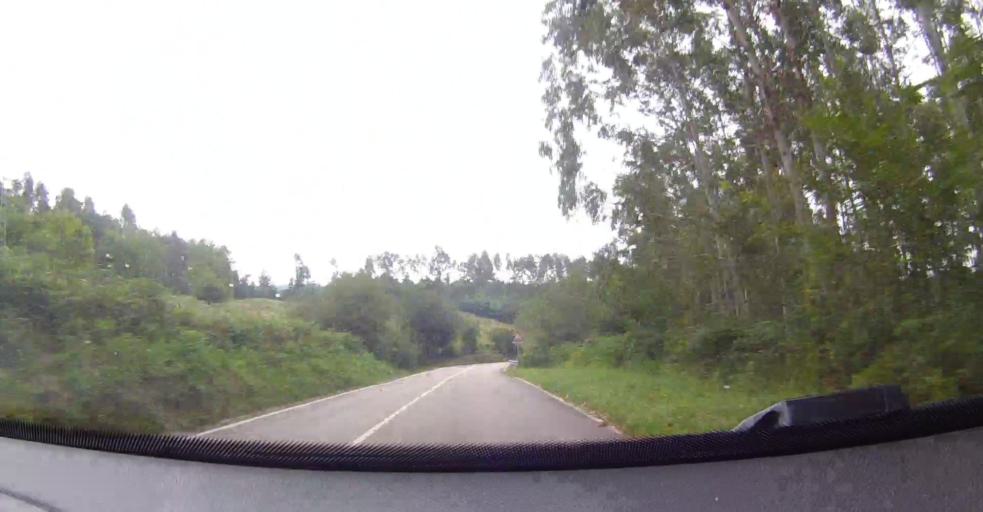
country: ES
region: Basque Country
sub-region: Bizkaia
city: Balmaseda
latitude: 43.2353
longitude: -3.2918
